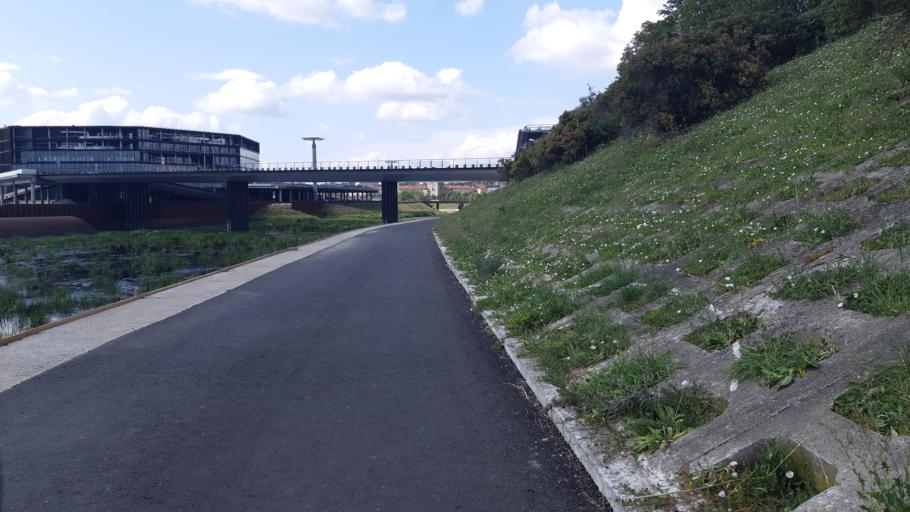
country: LT
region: Kauno apskritis
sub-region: Kaunas
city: Aleksotas
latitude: 54.8883
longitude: 23.9190
